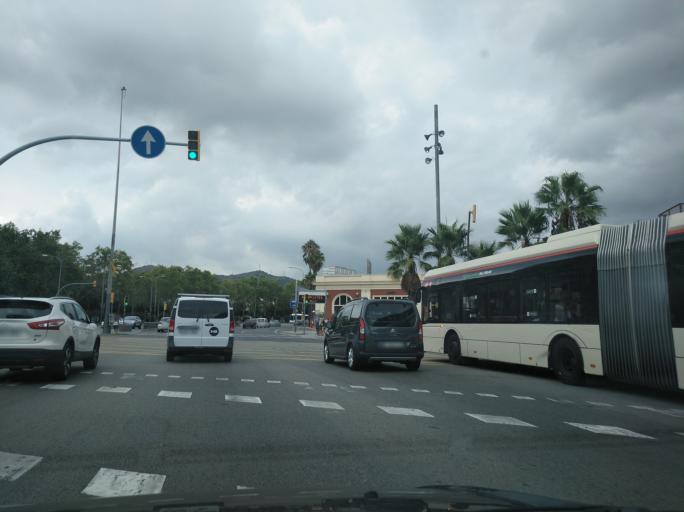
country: ES
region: Catalonia
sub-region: Provincia de Barcelona
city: Sant Andreu de Palomar
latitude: 41.4300
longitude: 2.1834
